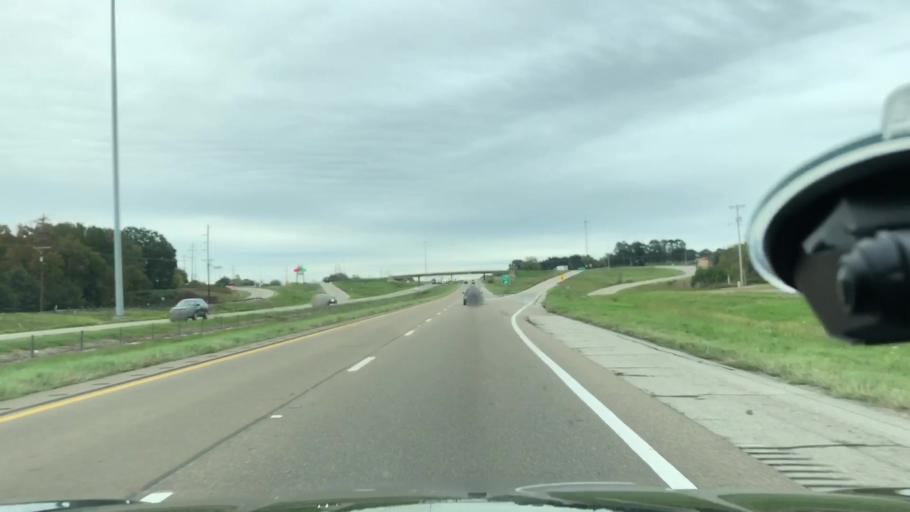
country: US
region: Texas
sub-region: Franklin County
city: Mount Vernon
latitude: 33.1605
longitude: -95.1184
